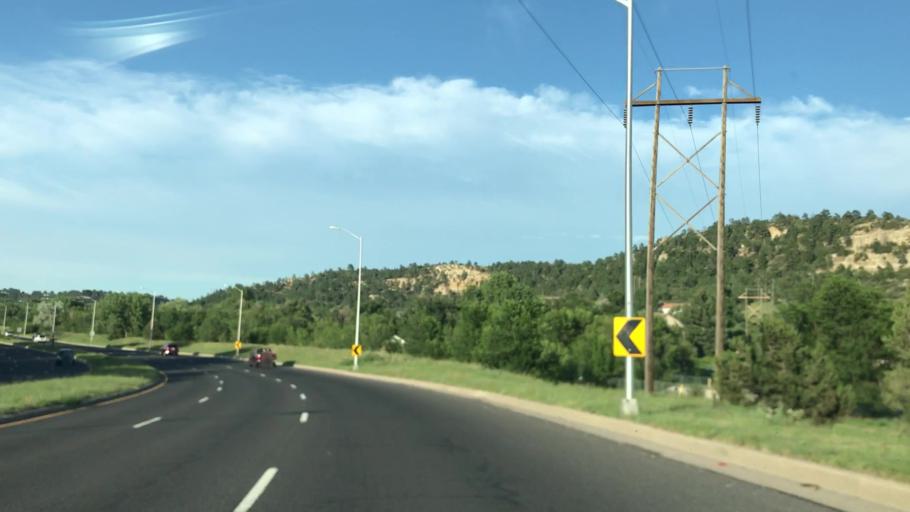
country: US
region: Colorado
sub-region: El Paso County
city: Colorado Springs
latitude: 38.8825
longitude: -104.7911
